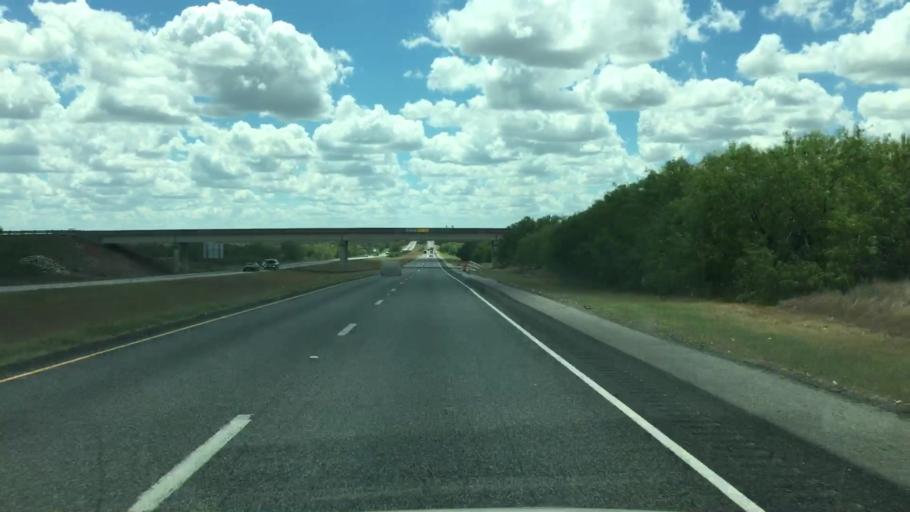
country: US
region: Texas
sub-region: Atascosa County
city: Pleasanton
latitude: 28.9770
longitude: -98.4342
